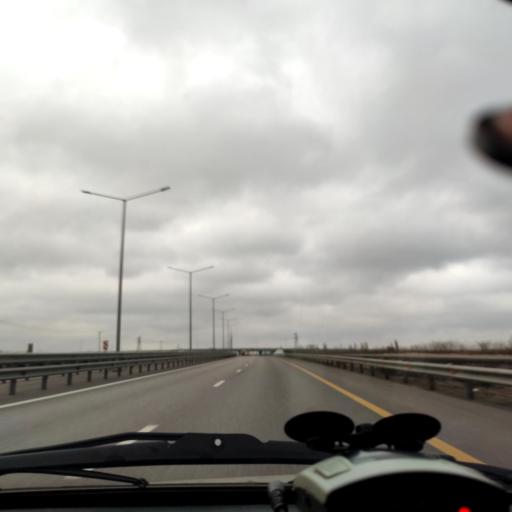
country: RU
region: Voronezj
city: Novaya Usman'
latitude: 51.5920
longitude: 39.3674
